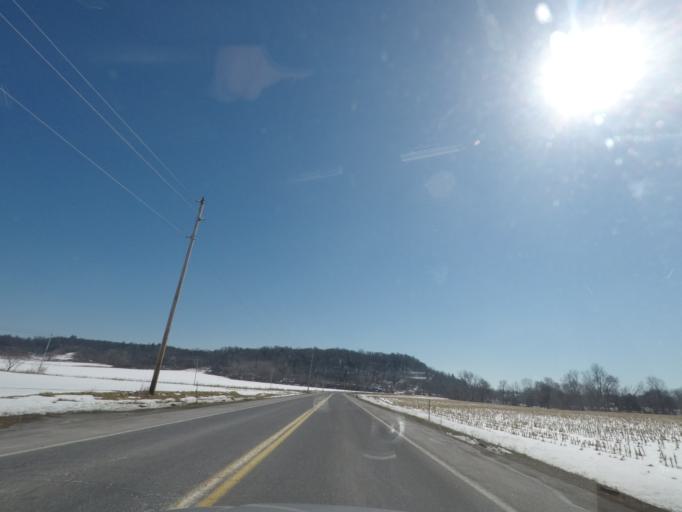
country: US
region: New York
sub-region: Saratoga County
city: Stillwater
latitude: 42.9355
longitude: -73.6476
